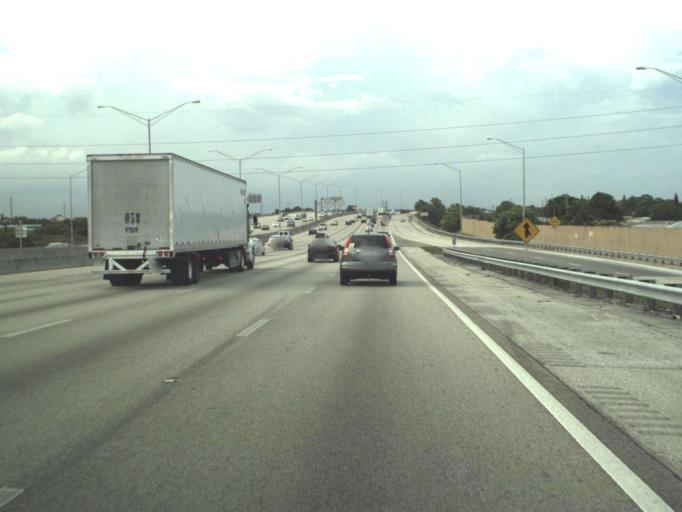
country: US
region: Florida
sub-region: Palm Beach County
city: Delray Beach
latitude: 26.4643
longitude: -80.0885
